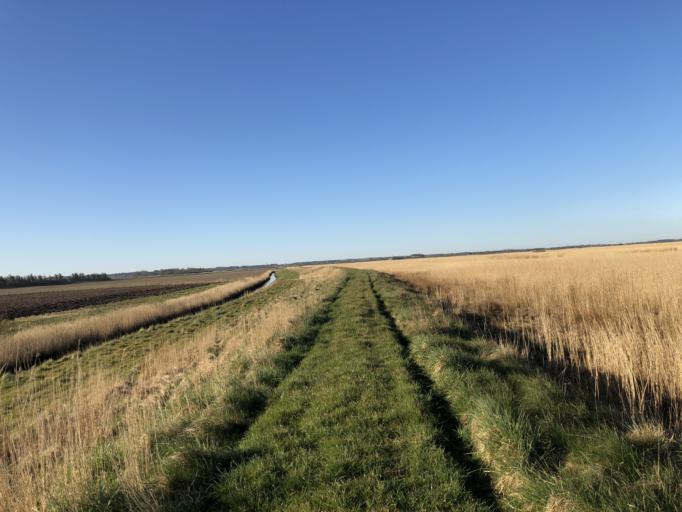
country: DK
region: Central Jutland
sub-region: Holstebro Kommune
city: Ulfborg
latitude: 56.3078
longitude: 8.2927
